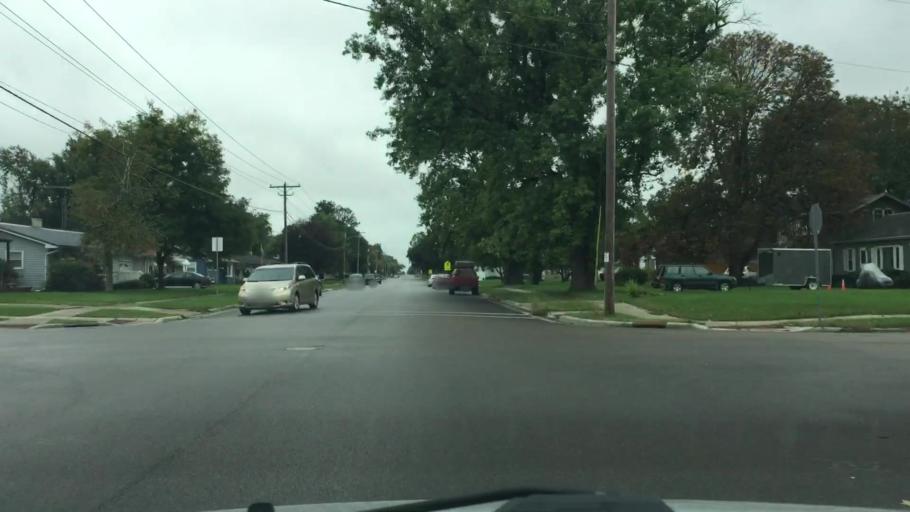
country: US
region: Wisconsin
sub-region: Rock County
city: Janesville
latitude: 42.6572
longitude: -89.0412
